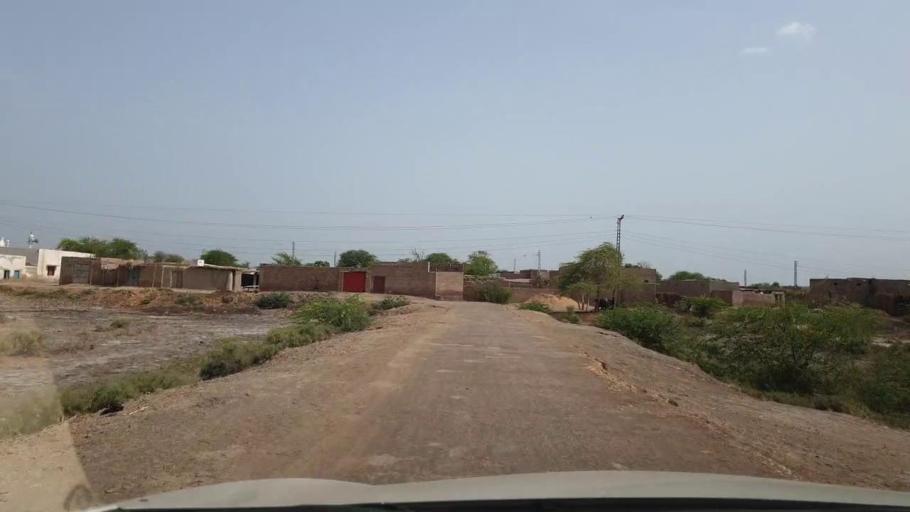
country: PK
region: Sindh
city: Mirwah Gorchani
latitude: 25.2770
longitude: 68.9583
